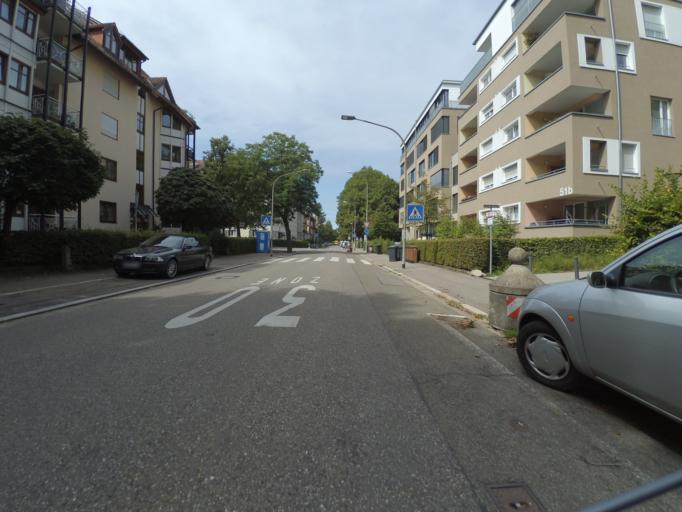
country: DE
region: Baden-Wuerttemberg
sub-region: Freiburg Region
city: Freiburg
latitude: 47.9916
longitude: 7.8630
